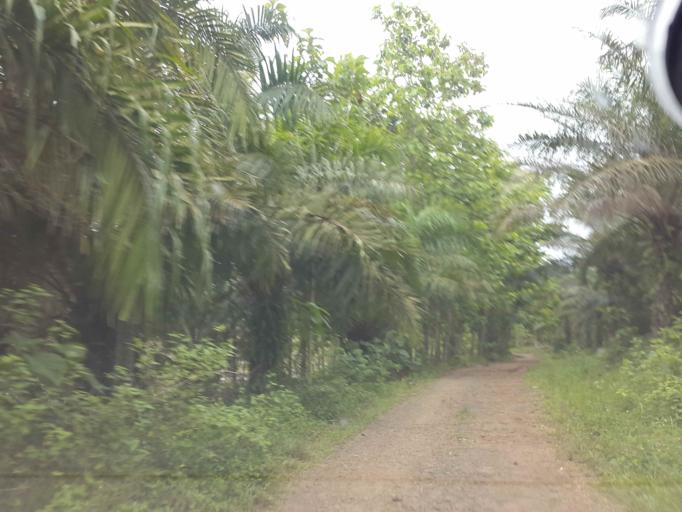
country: ID
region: Lampung
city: Sidorejo
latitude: -5.5537
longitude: 105.5195
